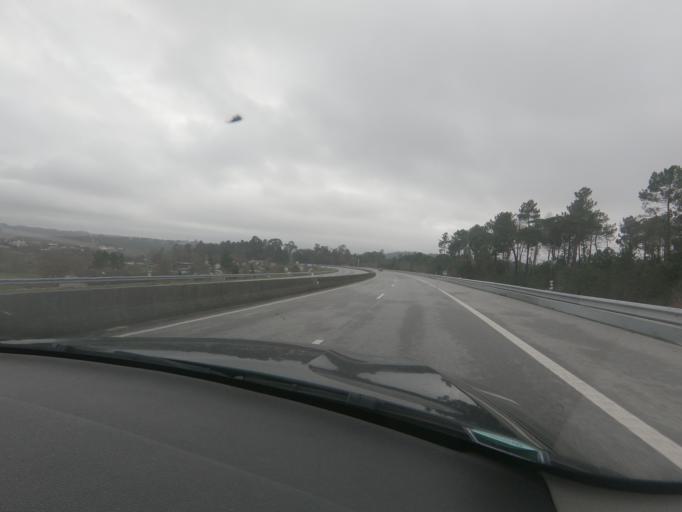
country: PT
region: Viseu
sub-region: Viseu
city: Abraveses
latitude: 40.6647
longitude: -7.9714
